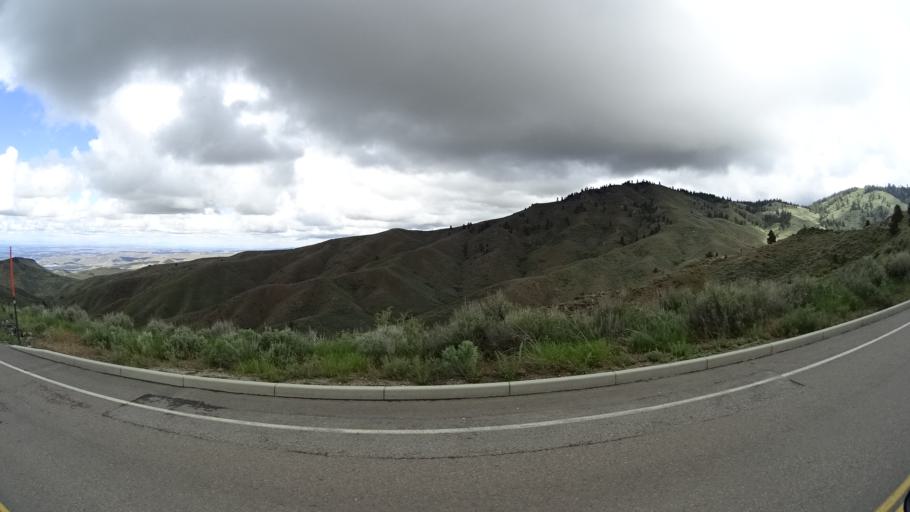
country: US
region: Idaho
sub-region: Ada County
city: Boise
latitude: 43.7240
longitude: -116.1587
